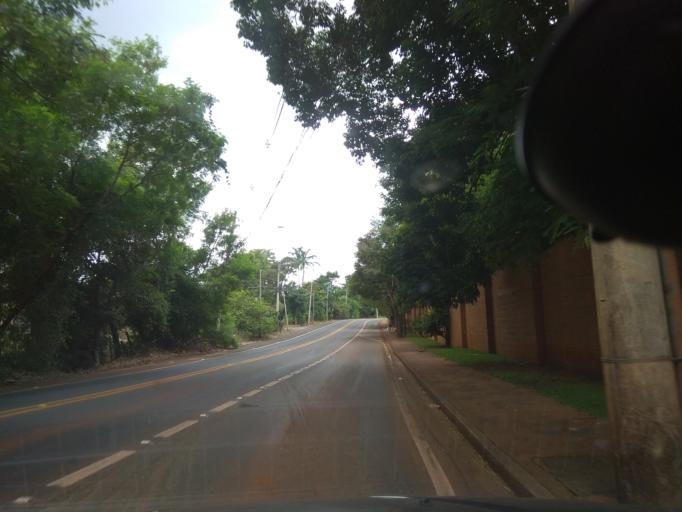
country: BR
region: Sao Paulo
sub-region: Paulinia
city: Paulinia
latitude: -22.7928
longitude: -47.0806
